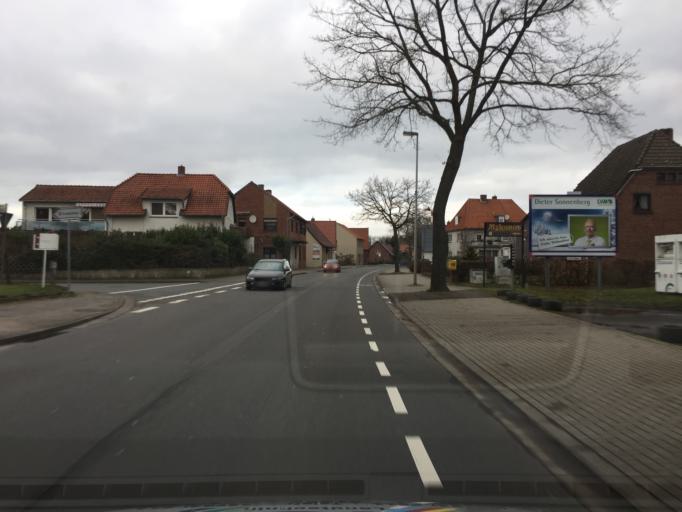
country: DE
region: Lower Saxony
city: Stolzenau
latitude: 52.5176
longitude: 9.0750
